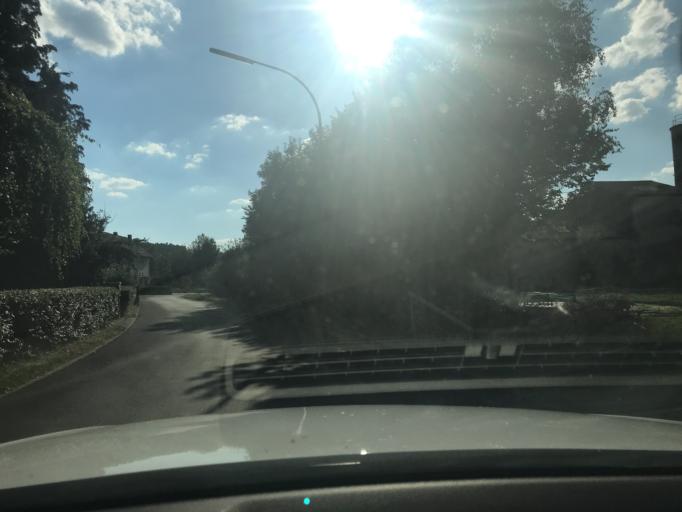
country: DE
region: Bavaria
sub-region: Upper Franconia
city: Pegnitz
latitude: 49.7446
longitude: 11.5605
